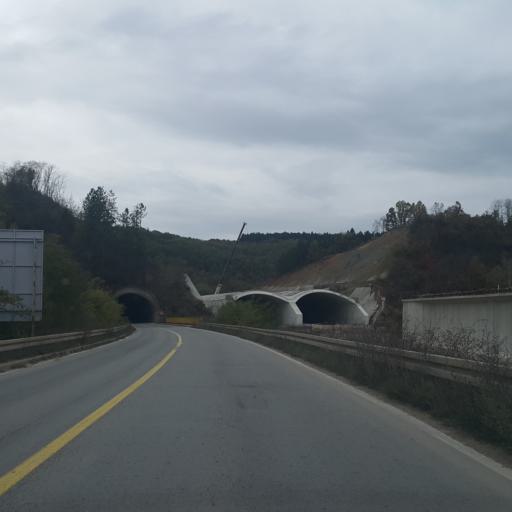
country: RS
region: Central Serbia
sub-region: Pirotski Okrug
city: Pirot
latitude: 43.2170
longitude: 22.5425
